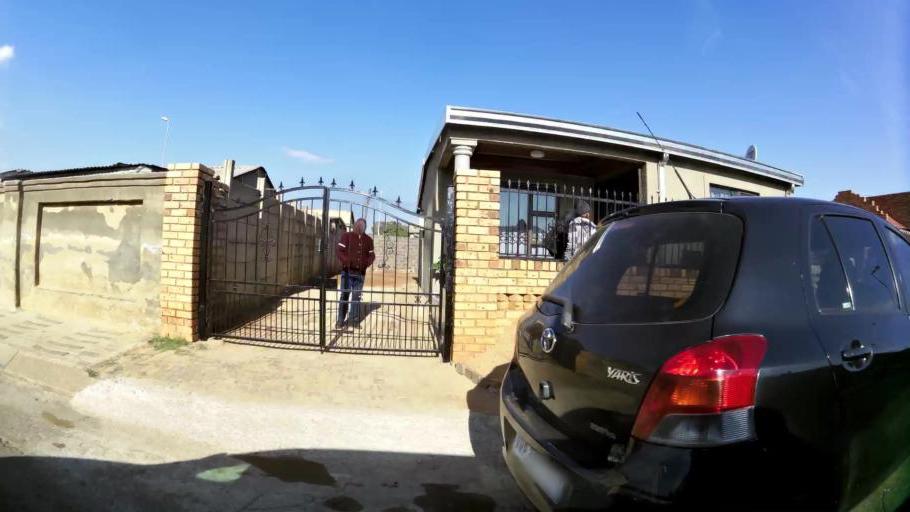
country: ZA
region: Gauteng
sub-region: City of Johannesburg Metropolitan Municipality
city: Soweto
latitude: -26.2550
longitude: 27.9164
